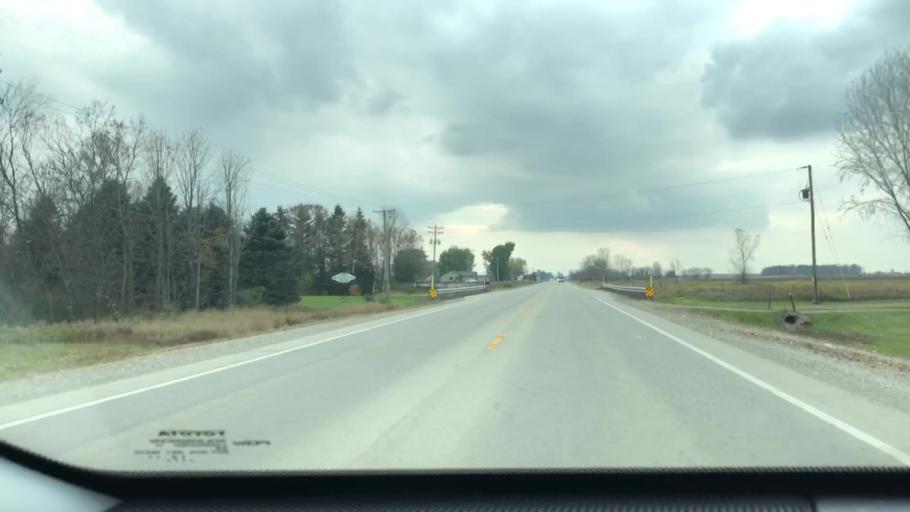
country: US
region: Wisconsin
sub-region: Outagamie County
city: Seymour
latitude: 44.5011
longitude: -88.2762
